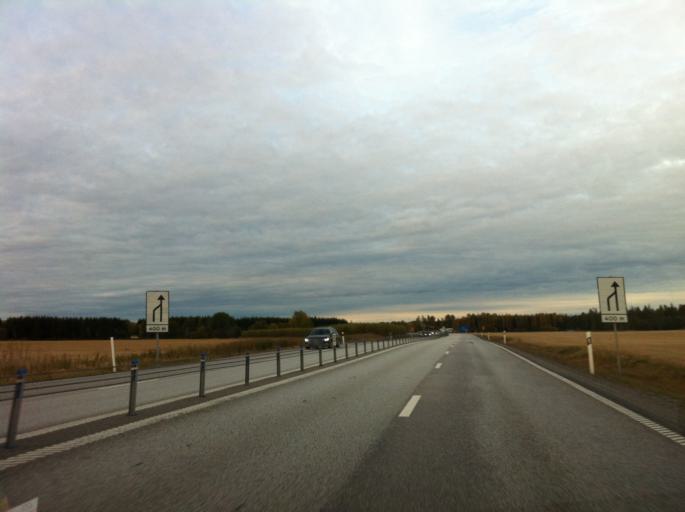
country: SE
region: OErebro
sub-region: Orebro Kommun
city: Hovsta
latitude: 59.4030
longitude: 15.1873
